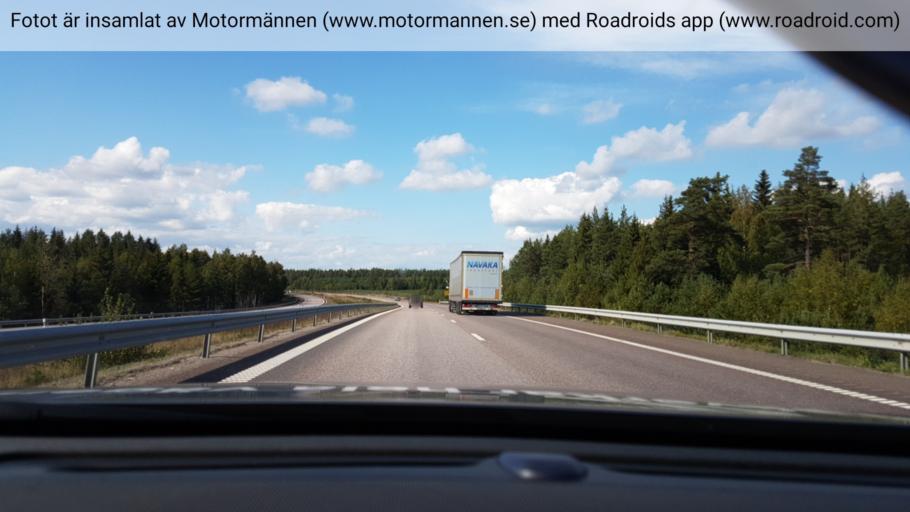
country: SE
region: Soedermanland
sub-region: Nykopings Kommun
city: Svalsta
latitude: 58.7529
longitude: 16.8733
